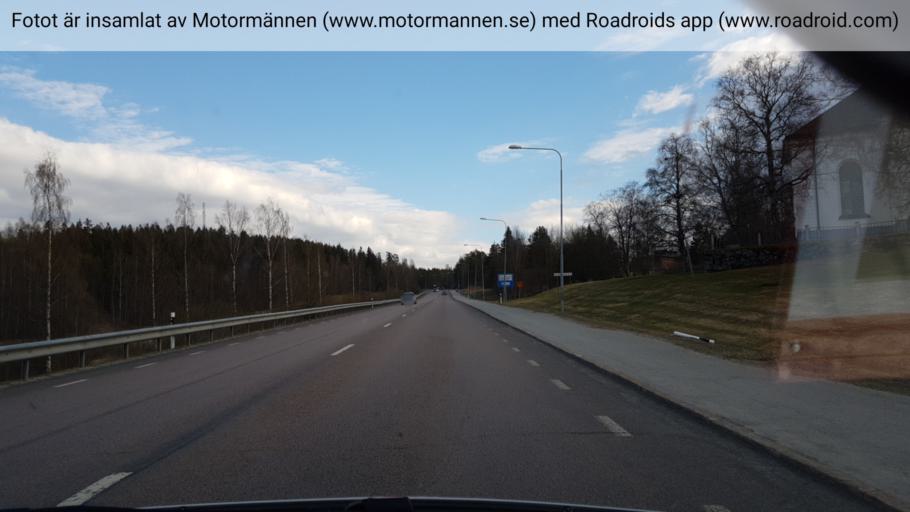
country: SE
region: Vaesternorrland
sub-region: Kramfors Kommun
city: Kramfors
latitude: 62.9178
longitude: 17.7865
